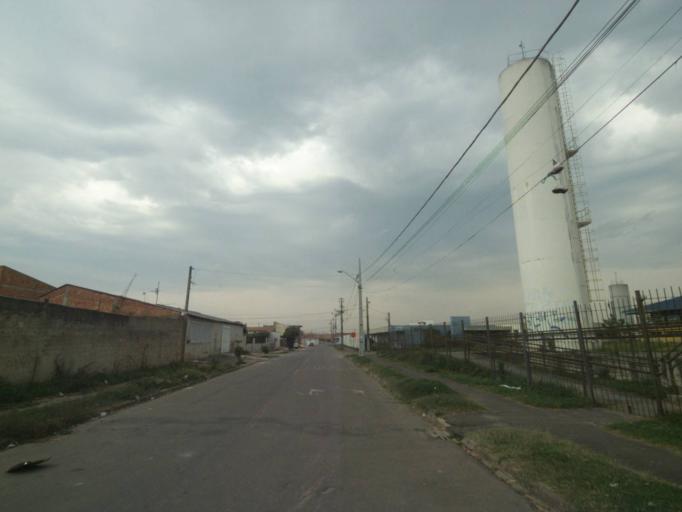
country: BR
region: Parana
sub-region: Sao Jose Dos Pinhais
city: Sao Jose dos Pinhais
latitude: -25.4970
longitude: -49.2013
